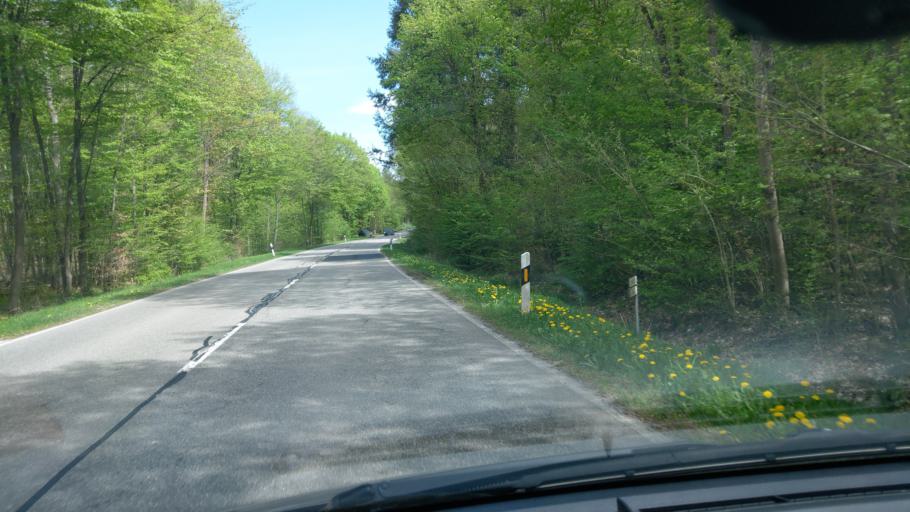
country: DE
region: Saarland
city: Spiesen-Elversberg
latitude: 49.2975
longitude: 7.1324
